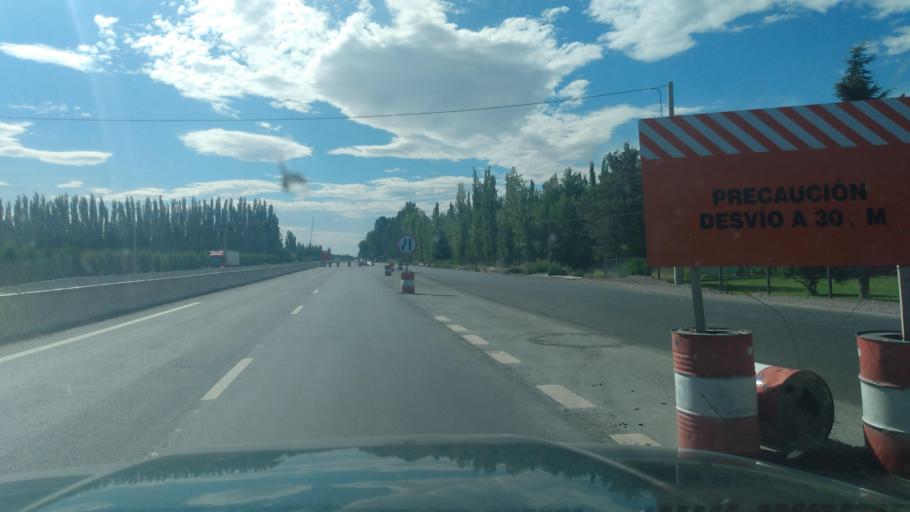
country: AR
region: Rio Negro
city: General Fernandez Oro
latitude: -38.9759
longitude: -67.9441
